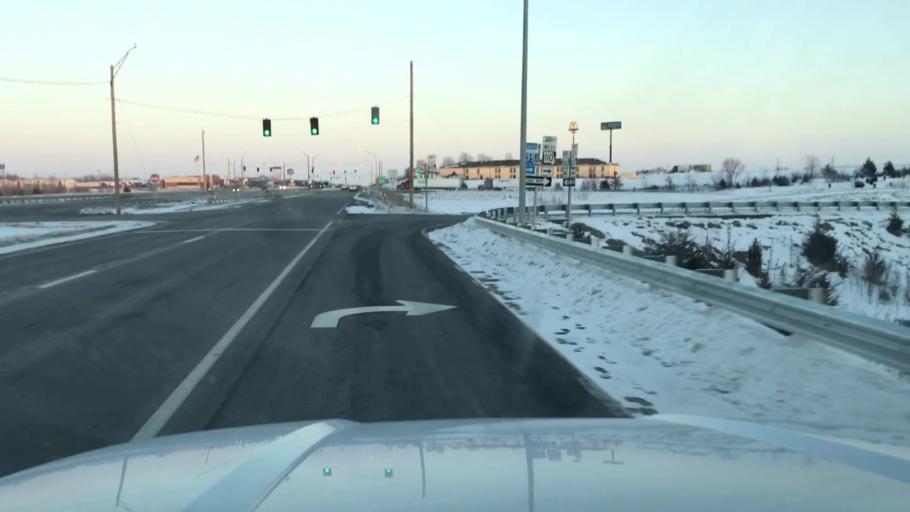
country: US
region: Missouri
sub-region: Clinton County
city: Cameron
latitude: 39.7537
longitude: -94.2219
